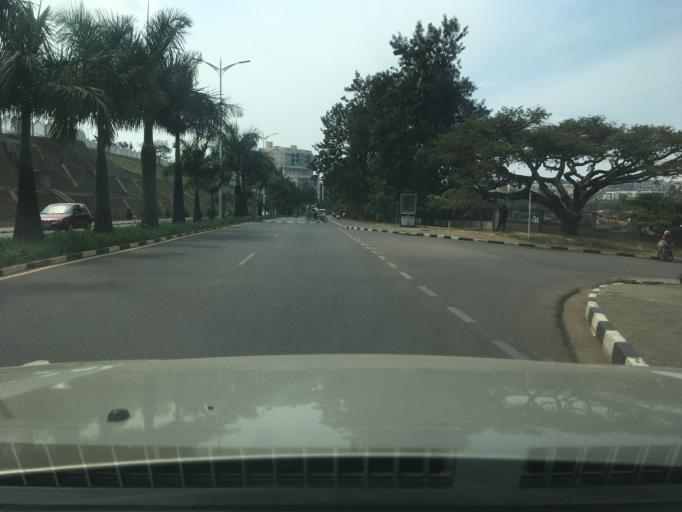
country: RW
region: Kigali
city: Kigali
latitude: -1.9535
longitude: 30.0982
